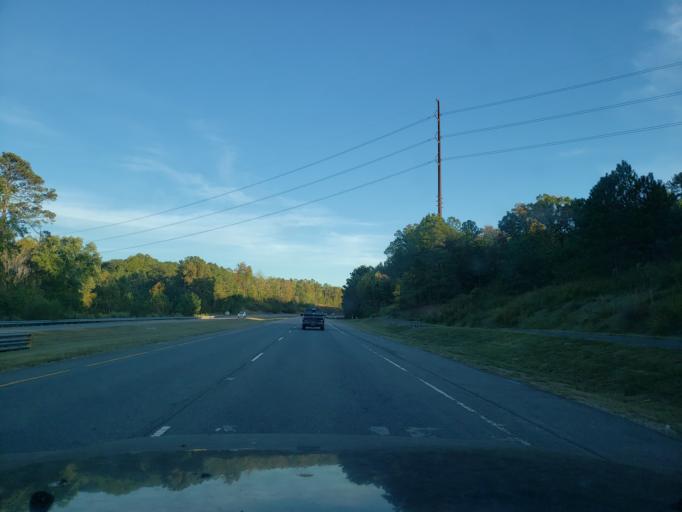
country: US
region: North Carolina
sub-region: Wake County
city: Morrisville
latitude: 35.8510
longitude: -78.8620
